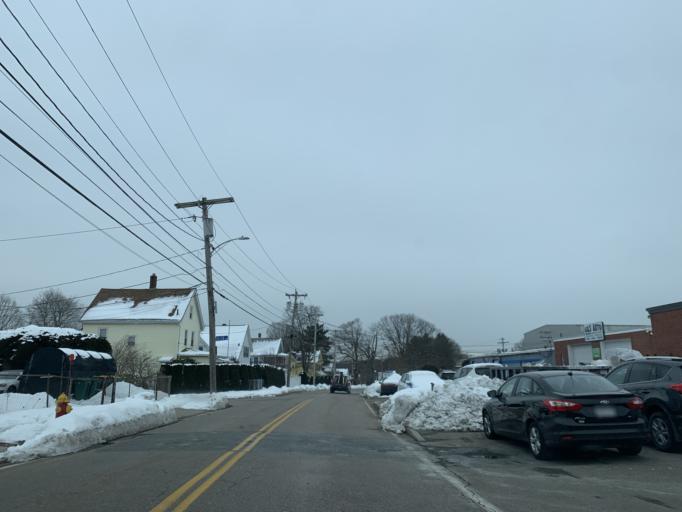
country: US
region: Massachusetts
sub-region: Norfolk County
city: Norwood
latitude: 42.1859
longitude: -71.1988
